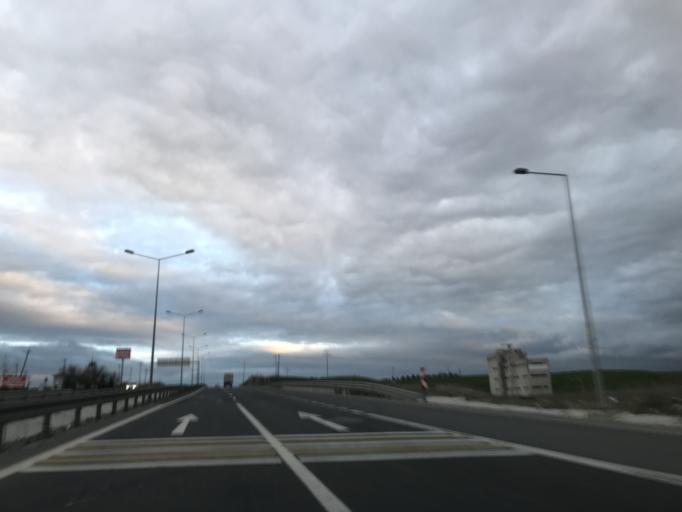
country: TR
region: Ankara
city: Ikizce
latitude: 39.6001
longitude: 32.8465
